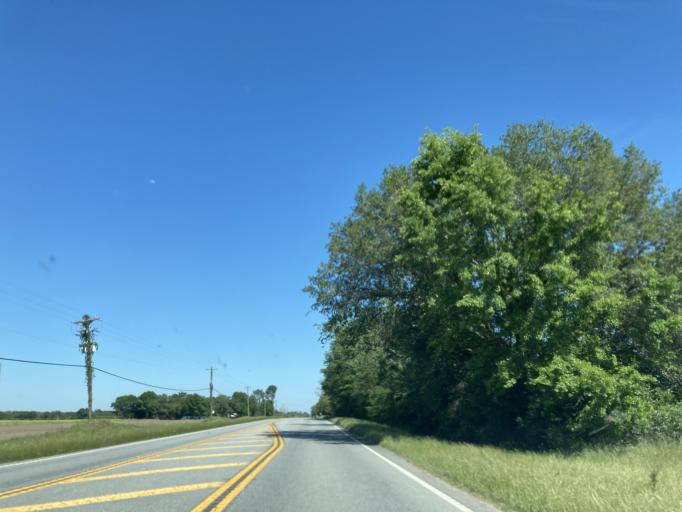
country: US
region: Georgia
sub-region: Miller County
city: Colquitt
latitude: 31.1853
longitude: -84.6024
